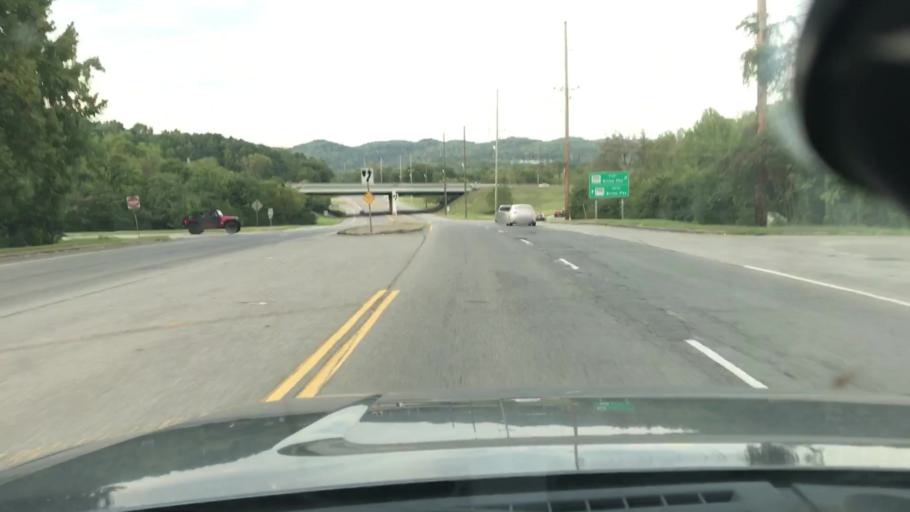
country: US
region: Tennessee
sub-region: Davidson County
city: Nashville
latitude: 36.2267
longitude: -86.8361
